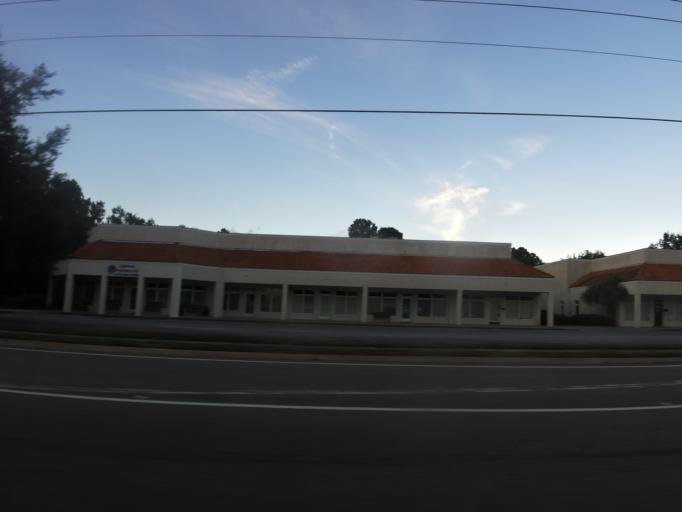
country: US
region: Georgia
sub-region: Camden County
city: St. Marys
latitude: 30.7440
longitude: -81.5559
